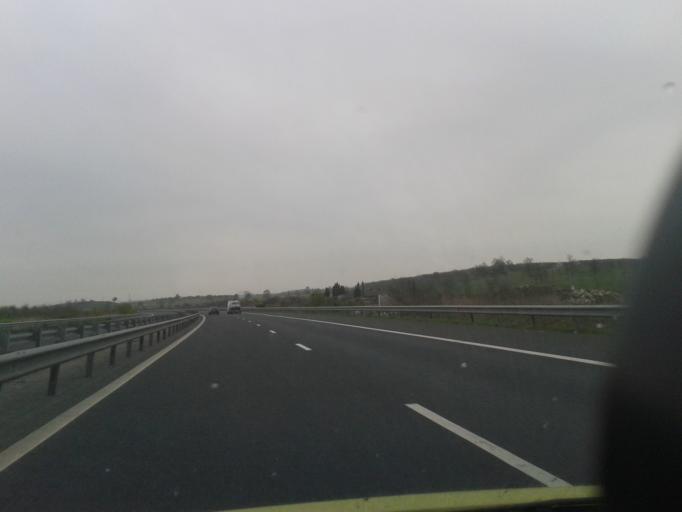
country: RO
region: Hunedoara
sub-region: Comuna Turdas
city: Turdas
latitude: 45.8369
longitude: 23.1010
